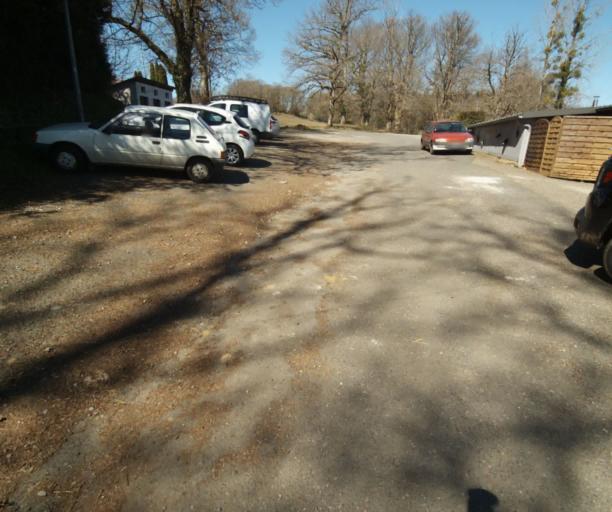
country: FR
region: Limousin
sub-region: Departement de la Correze
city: Seilhac
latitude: 45.3771
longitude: 1.6943
